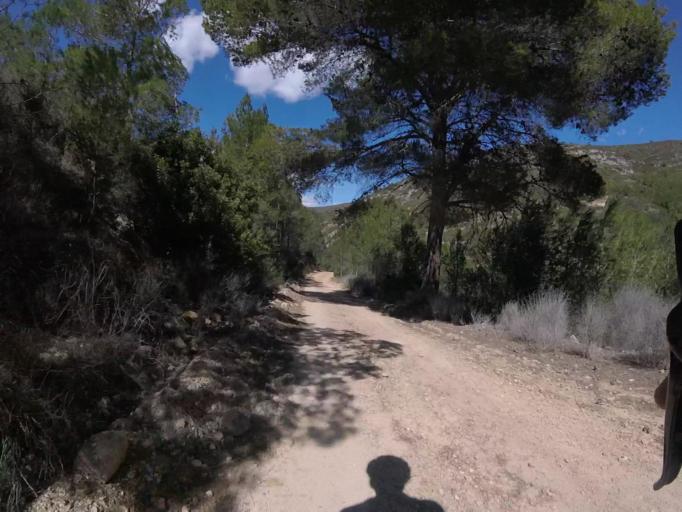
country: ES
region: Valencia
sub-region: Provincia de Castello
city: Cabanes
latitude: 40.1606
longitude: 0.1076
